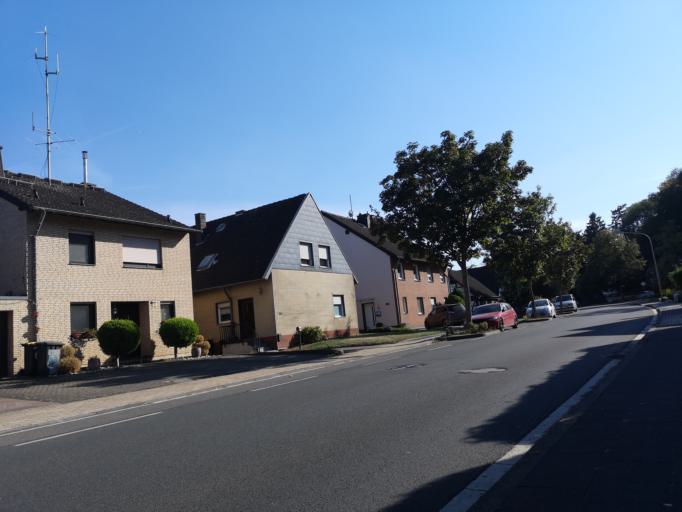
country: DE
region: North Rhine-Westphalia
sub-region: Regierungsbezirk Koln
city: Kreuzau
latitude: 50.7303
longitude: 6.4777
